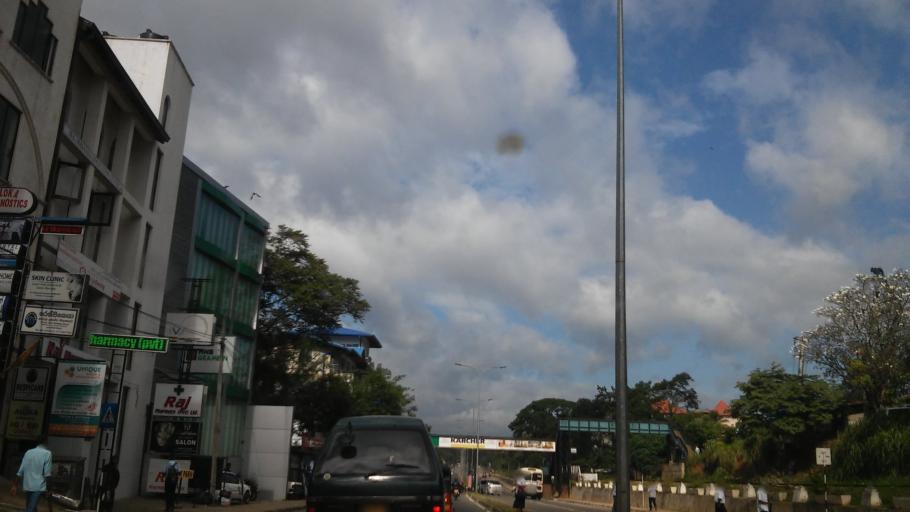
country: LK
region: Central
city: Kandy
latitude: 7.2743
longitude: 80.6127
